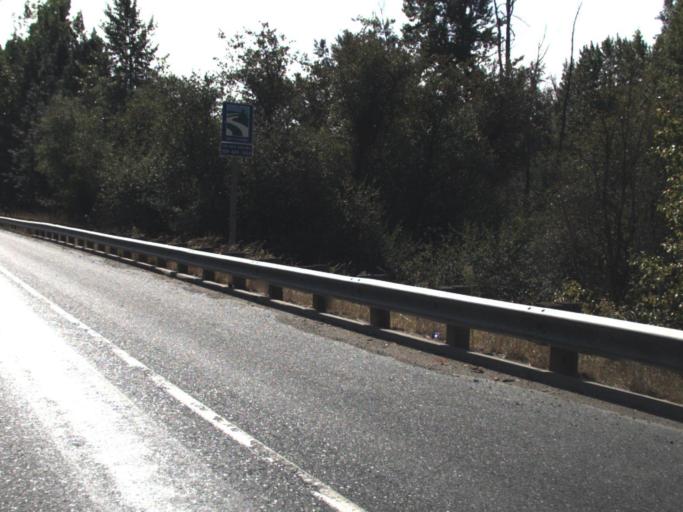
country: US
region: Washington
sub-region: Stevens County
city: Chewelah
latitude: 48.3312
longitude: -117.8277
